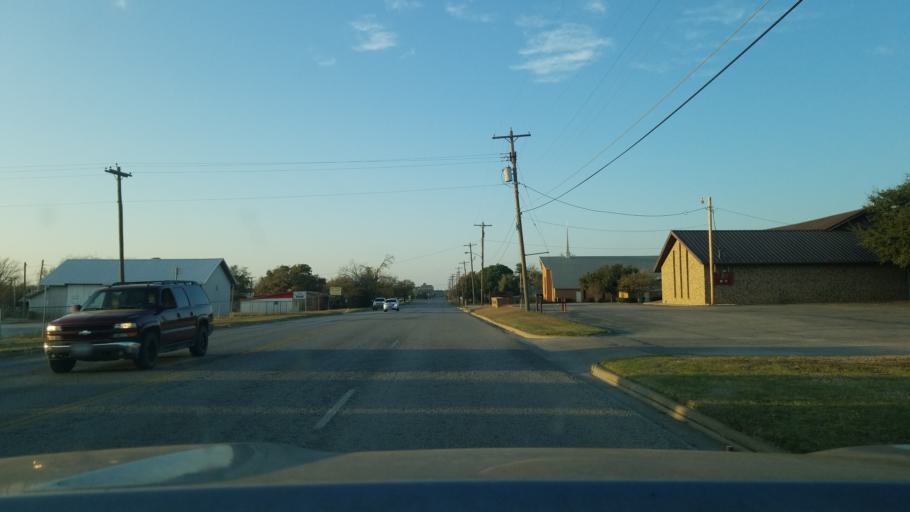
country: US
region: Texas
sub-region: Eastland County
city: Cisco
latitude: 32.3787
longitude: -98.9731
